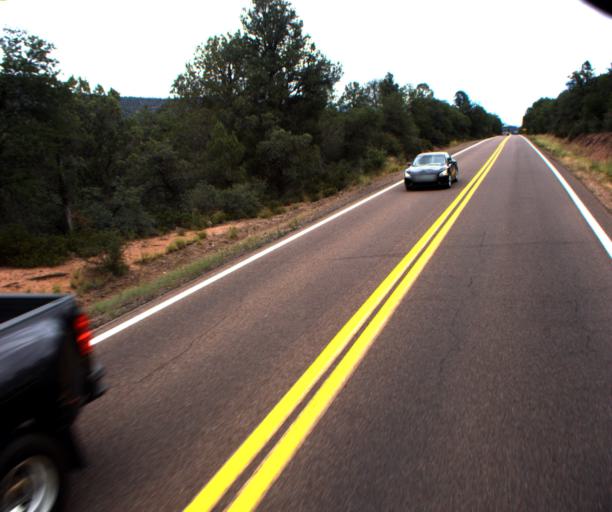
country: US
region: Arizona
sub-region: Gila County
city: Star Valley
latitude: 34.2622
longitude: -111.2024
